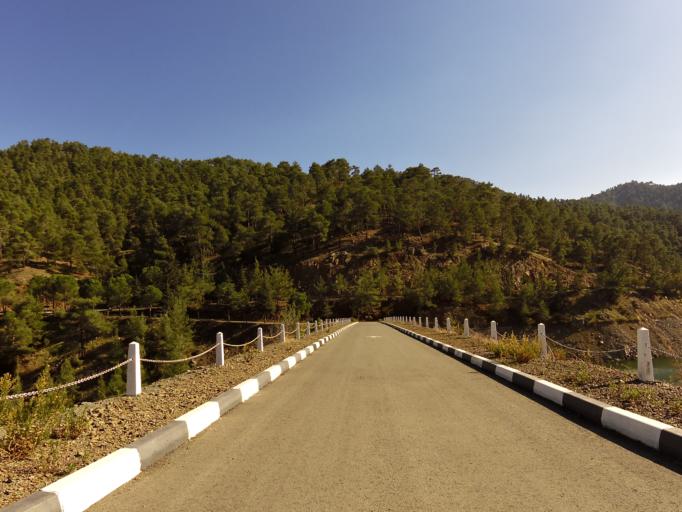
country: CY
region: Limassol
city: Kyperounta
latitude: 35.0091
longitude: 33.0370
